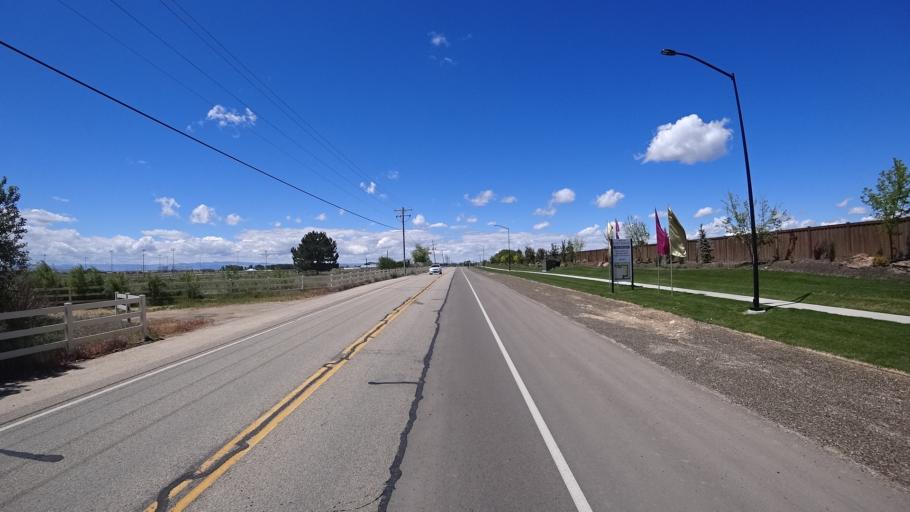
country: US
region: Idaho
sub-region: Ada County
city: Meridian
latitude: 43.5465
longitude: -116.3619
